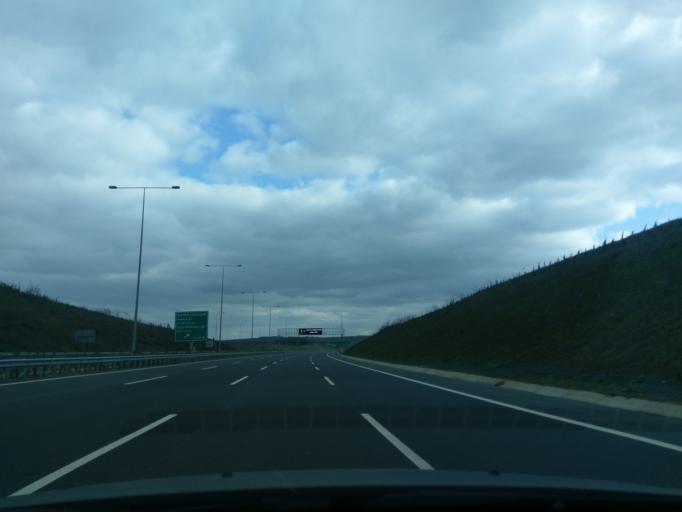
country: TR
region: Istanbul
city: Kemerburgaz
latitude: 41.2379
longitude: 28.8275
